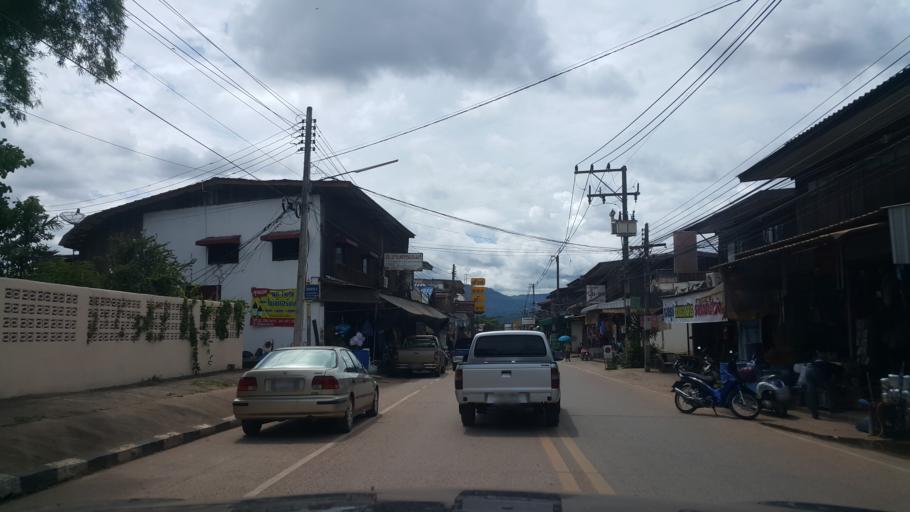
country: TH
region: Phitsanulok
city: Chat Trakan
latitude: 17.2752
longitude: 100.6030
